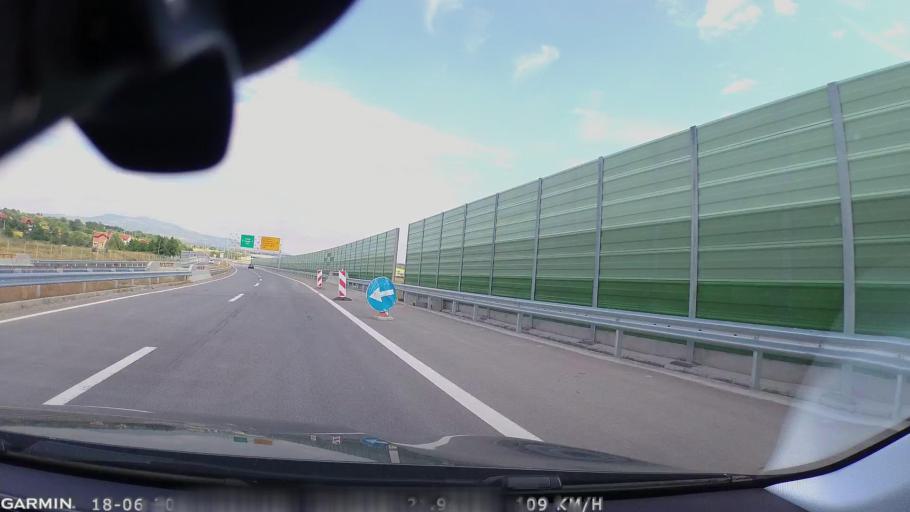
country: MK
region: Sveti Nikole
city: Sveti Nikole
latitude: 41.8743
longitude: 21.9452
